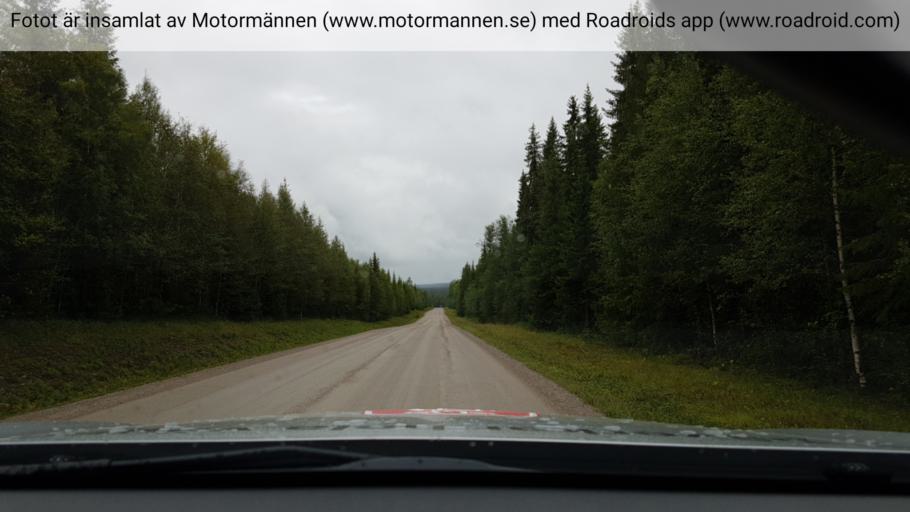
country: SE
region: Vaesterbotten
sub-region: Asele Kommun
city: Insjon
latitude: 64.7302
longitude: 17.6557
